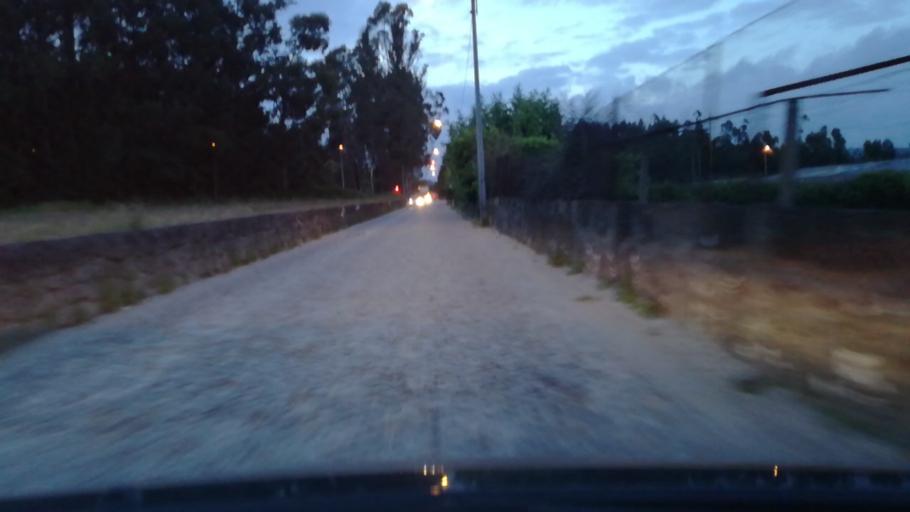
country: PT
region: Porto
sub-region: Maia
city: Anta
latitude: 41.2586
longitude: -8.6085
